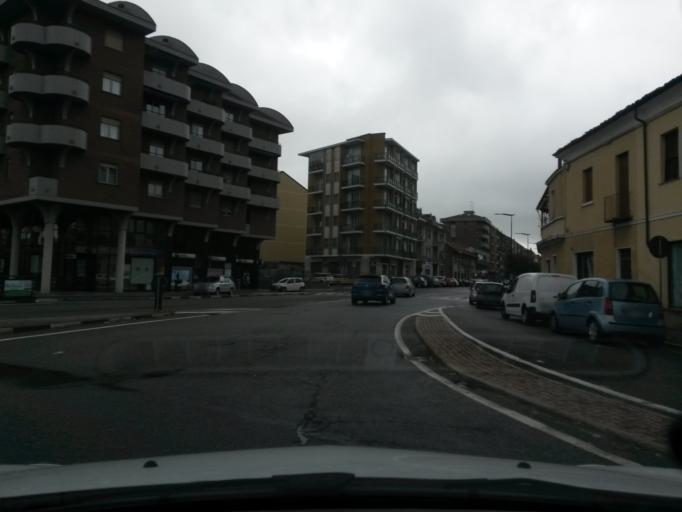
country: IT
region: Piedmont
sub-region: Provincia di Torino
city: Rivoli
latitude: 45.0755
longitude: 7.5196
